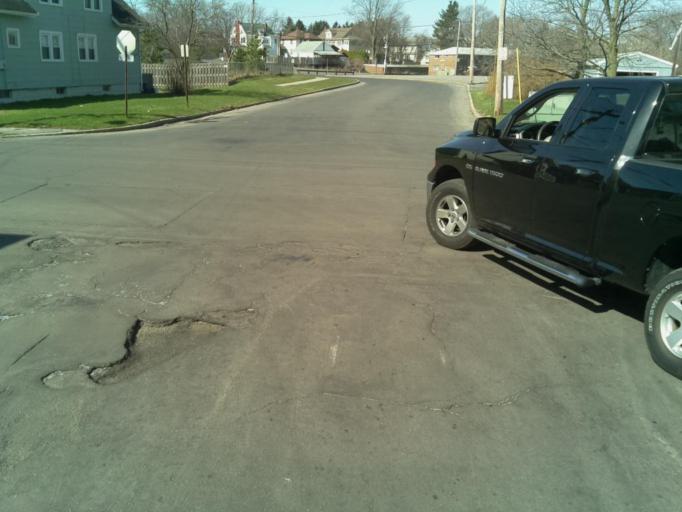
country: US
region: New York
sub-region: Onondaga County
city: Lyncourt
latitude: 43.0693
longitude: -76.1142
